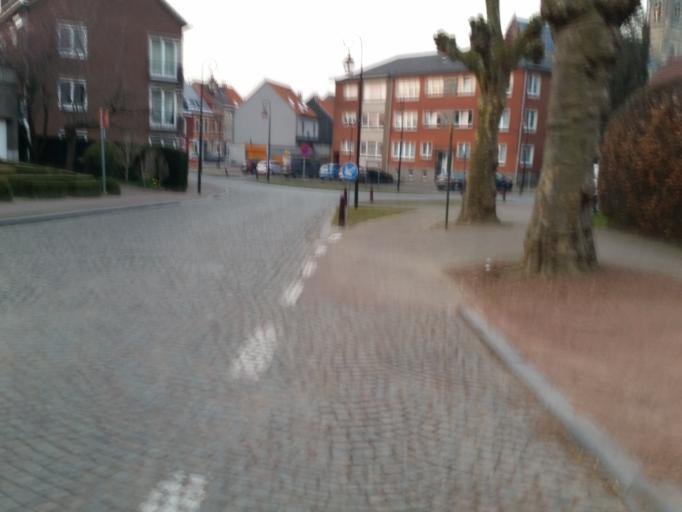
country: BE
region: Flanders
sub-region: Provincie Vlaams-Brabant
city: Grimbergen
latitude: 50.9317
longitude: 4.3691
